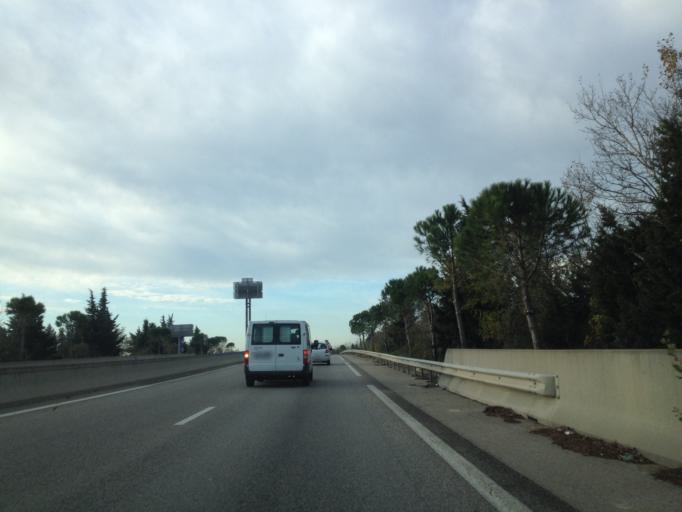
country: FR
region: Provence-Alpes-Cote d'Azur
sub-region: Departement du Vaucluse
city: Sorgues
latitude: 44.0129
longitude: 4.8661
